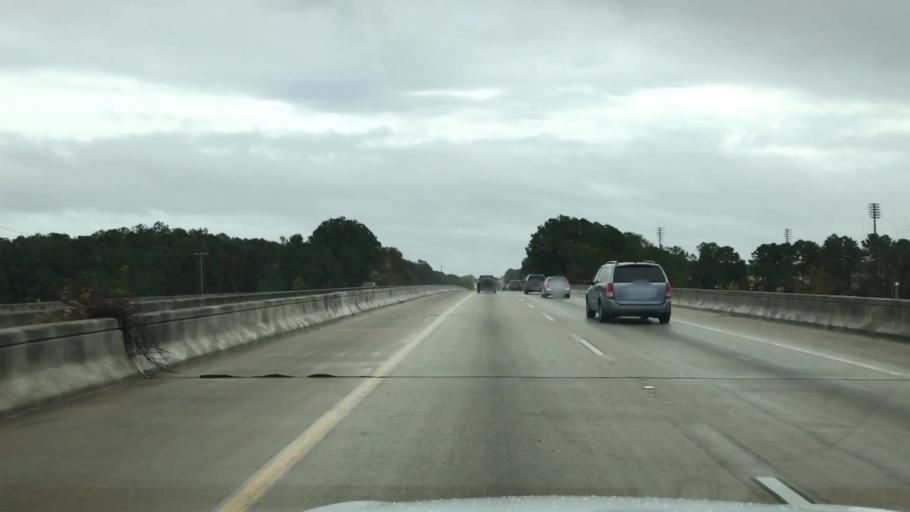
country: US
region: South Carolina
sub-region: Charleston County
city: North Charleston
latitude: 32.8734
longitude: -79.9225
